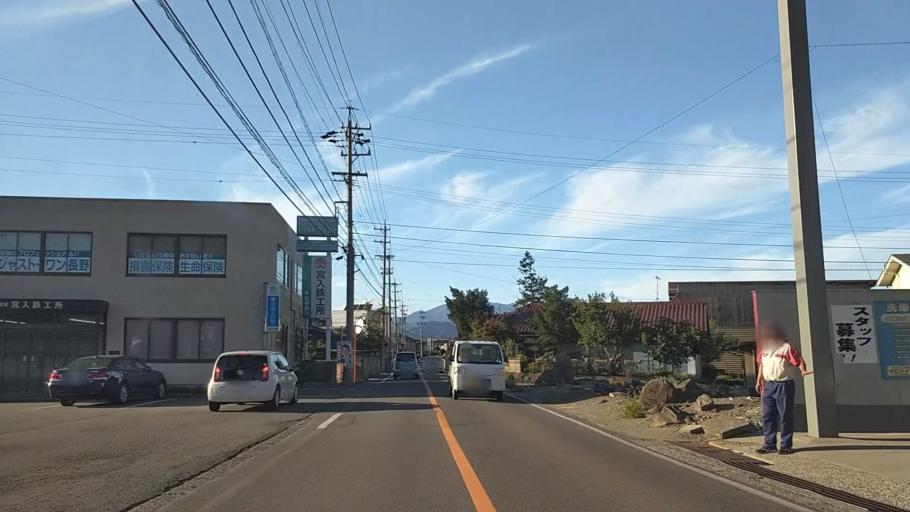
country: JP
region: Nagano
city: Nagano-shi
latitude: 36.5861
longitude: 138.1990
